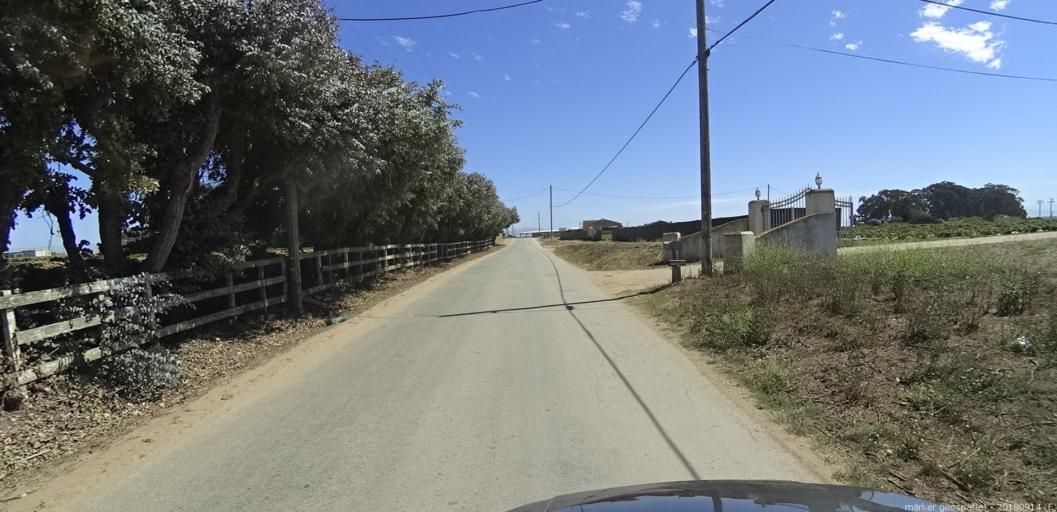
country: US
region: California
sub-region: Monterey County
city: Las Lomas
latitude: 36.8534
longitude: -121.7877
